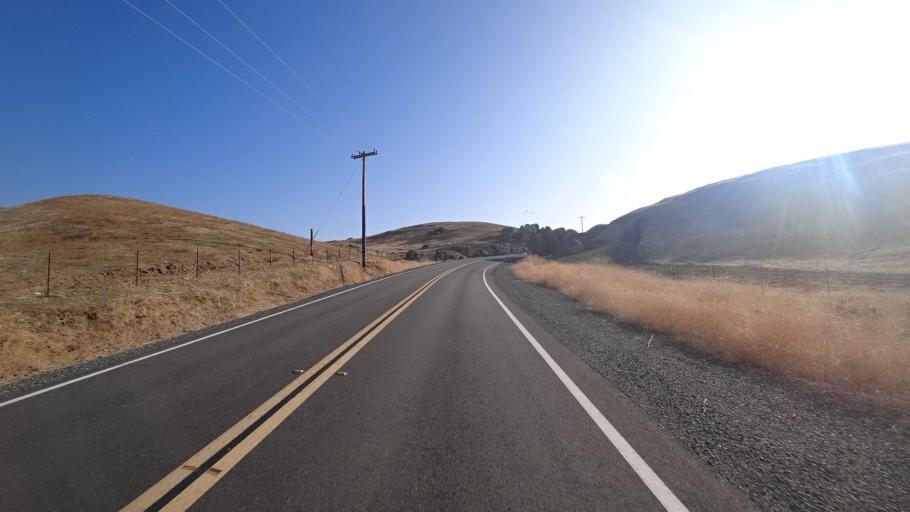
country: US
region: California
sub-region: Tulare County
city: Richgrove
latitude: 35.7429
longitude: -118.9011
